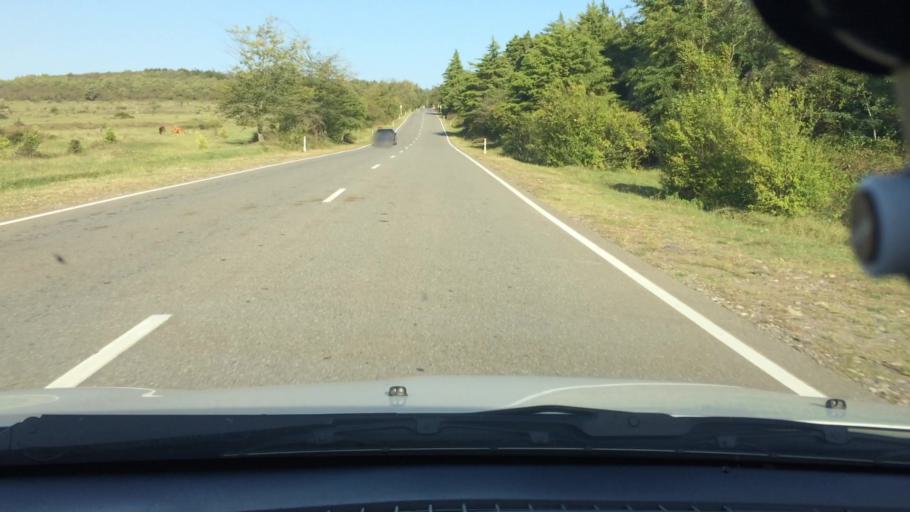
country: GE
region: Imereti
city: Kutaisi
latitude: 42.2419
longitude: 42.7635
